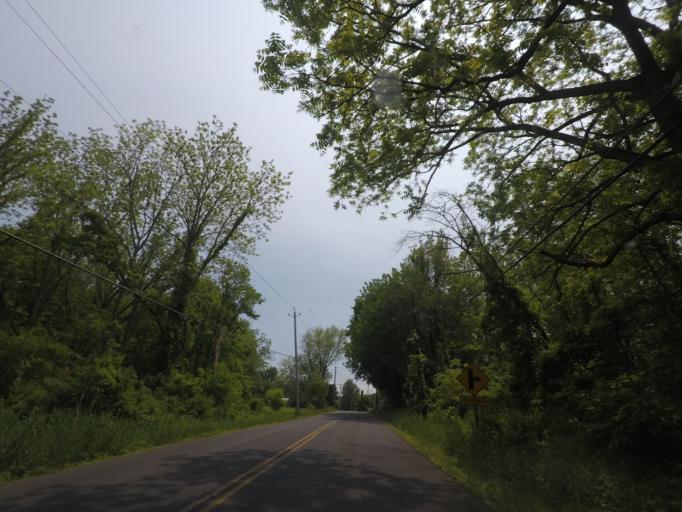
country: US
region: New York
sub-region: Rensselaer County
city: Castleton-on-Hudson
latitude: 42.5158
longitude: -73.7065
